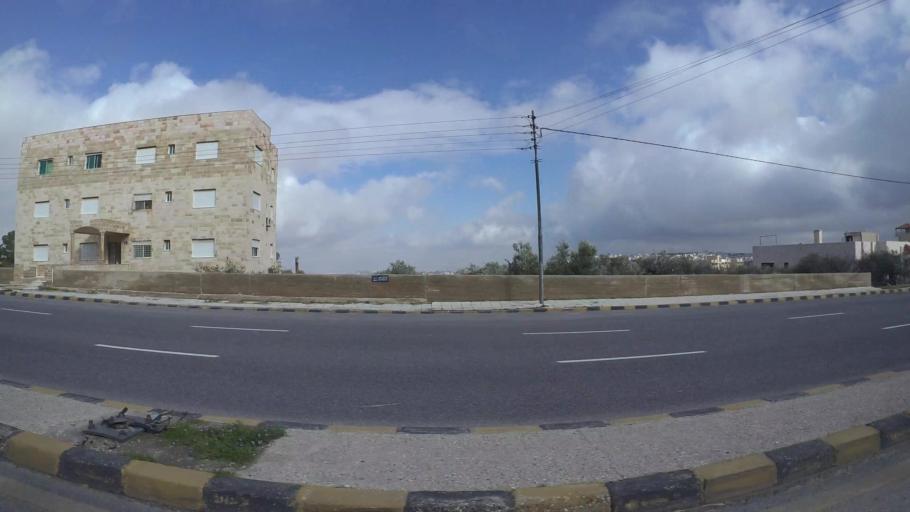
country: JO
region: Amman
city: Al Jubayhah
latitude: 32.0387
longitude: 35.8656
